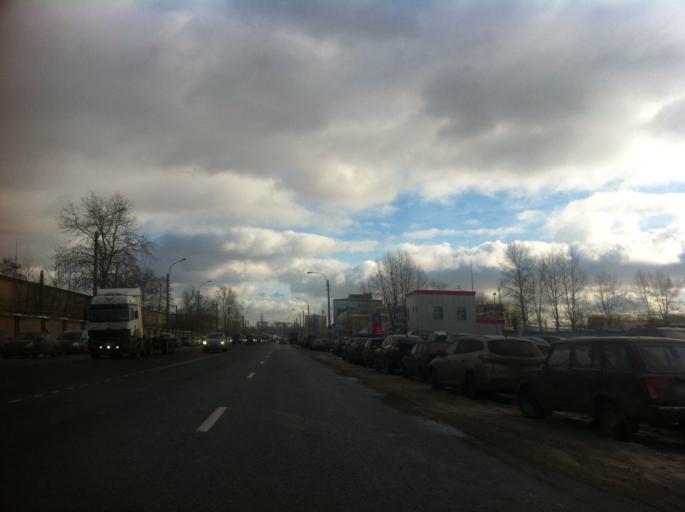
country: RU
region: St.-Petersburg
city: Avtovo
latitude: 59.8701
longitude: 30.2323
